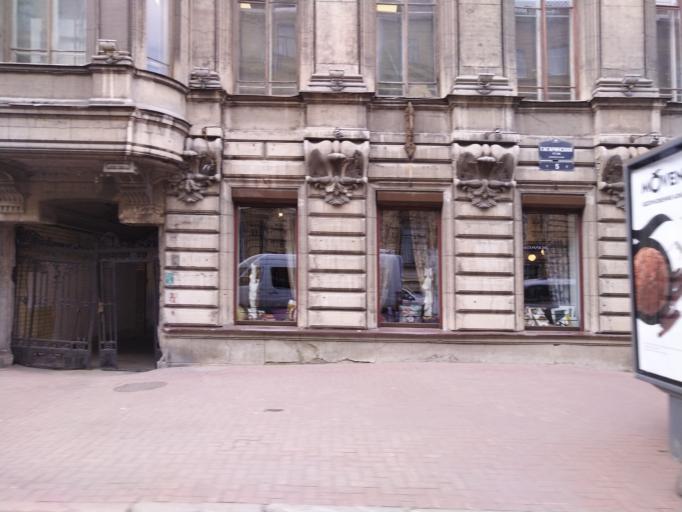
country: RU
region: St.-Petersburg
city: Centralniy
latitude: 59.9477
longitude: 30.3418
